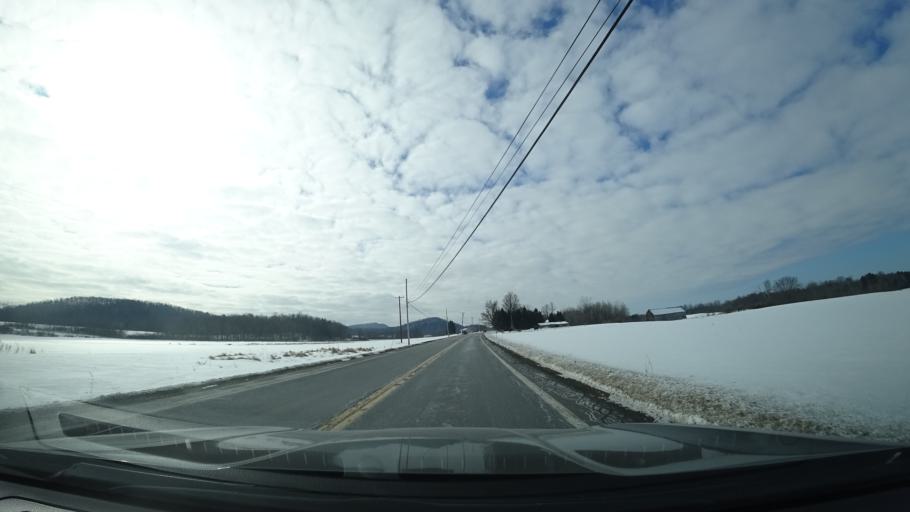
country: US
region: New York
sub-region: Washington County
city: Fort Edward
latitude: 43.2522
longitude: -73.4748
